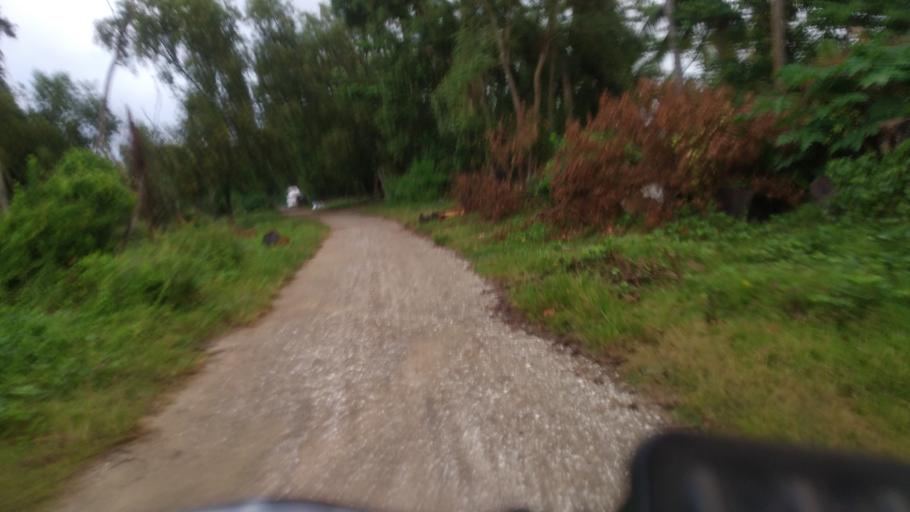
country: IN
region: Kerala
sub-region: Ernakulam
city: Cochin
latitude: 10.0096
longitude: 76.2175
